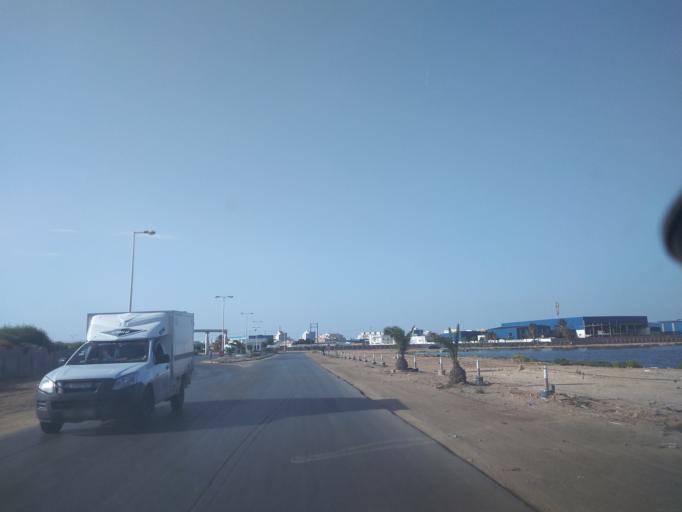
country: TN
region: Safaqis
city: Sfax
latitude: 34.7198
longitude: 10.7609
